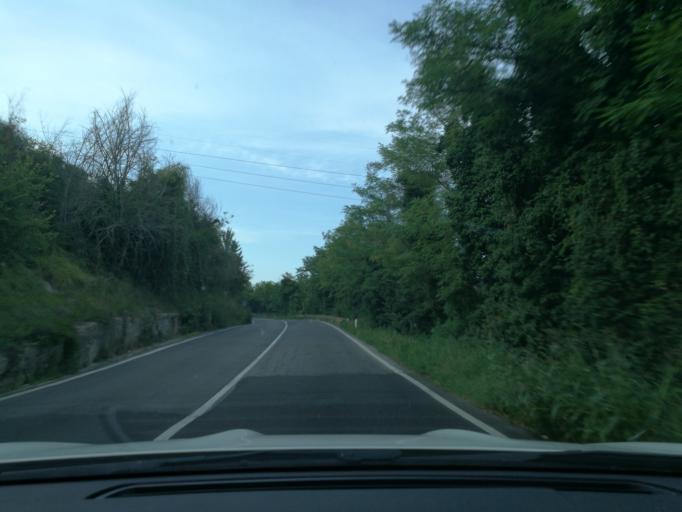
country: IT
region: Umbria
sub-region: Provincia di Terni
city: San Gemini
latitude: 42.6274
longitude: 12.5517
